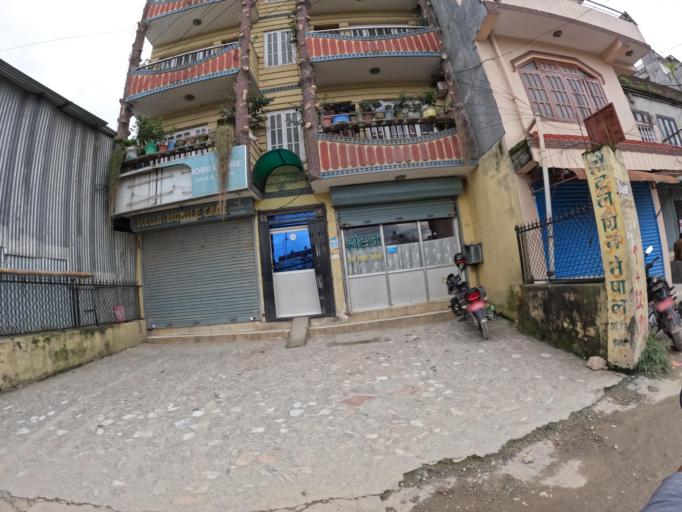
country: NP
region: Central Region
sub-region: Bagmati Zone
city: Kathmandu
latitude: 27.7377
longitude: 85.3092
